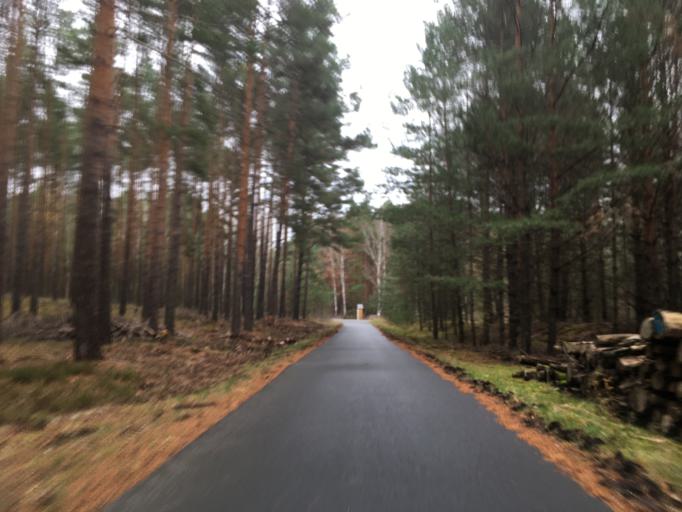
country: DE
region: Brandenburg
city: Mullrose
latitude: 52.2263
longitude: 14.4441
